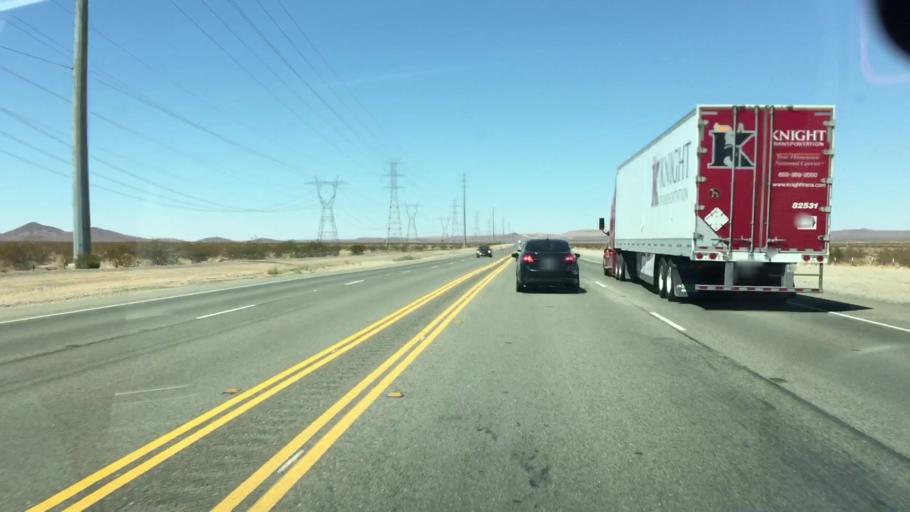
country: US
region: California
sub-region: San Bernardino County
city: Adelanto
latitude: 34.7644
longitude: -117.4752
